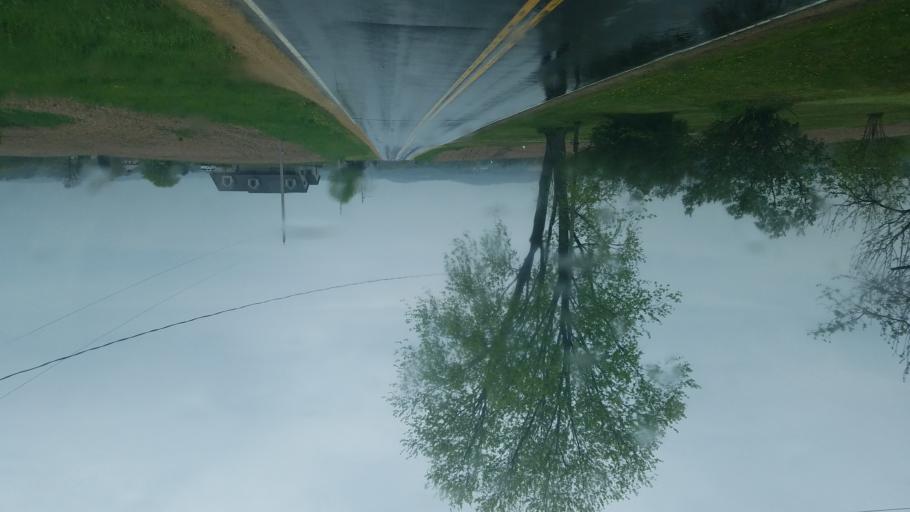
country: US
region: Wisconsin
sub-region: Vernon County
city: Hillsboro
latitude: 43.6512
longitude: -90.3253
